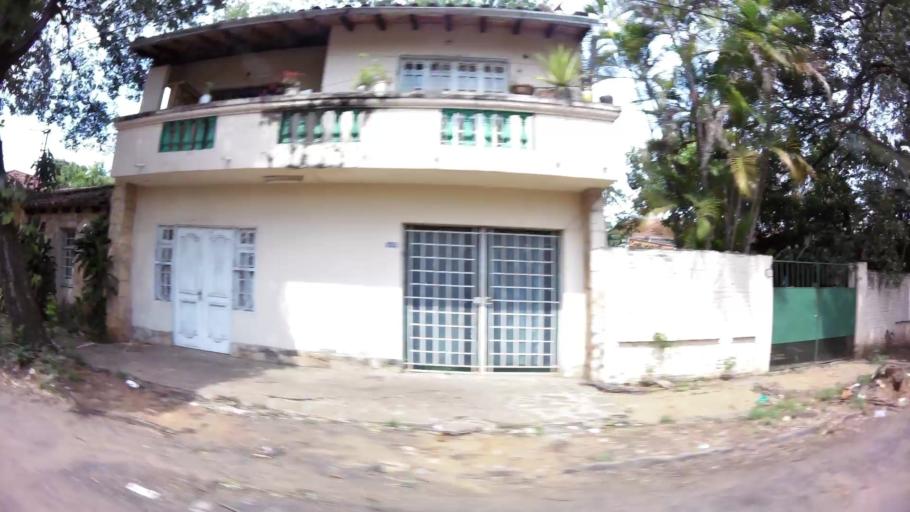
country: PY
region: Asuncion
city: Asuncion
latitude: -25.2810
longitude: -57.5691
